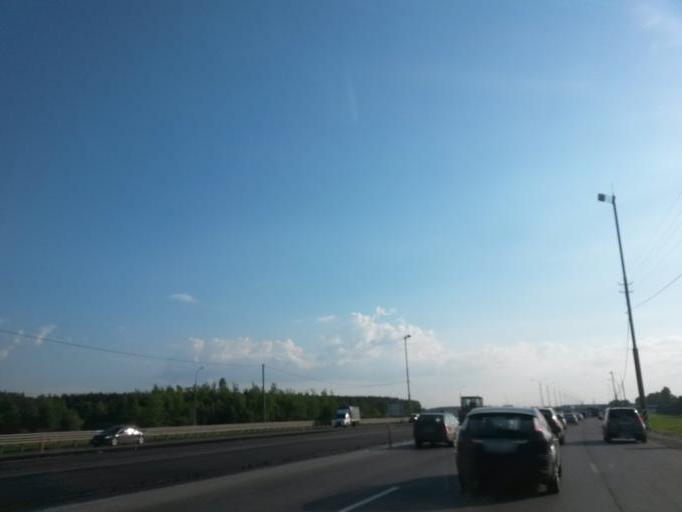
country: RU
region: Moskovskaya
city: Klimovsk
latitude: 55.3353
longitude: 37.5722
